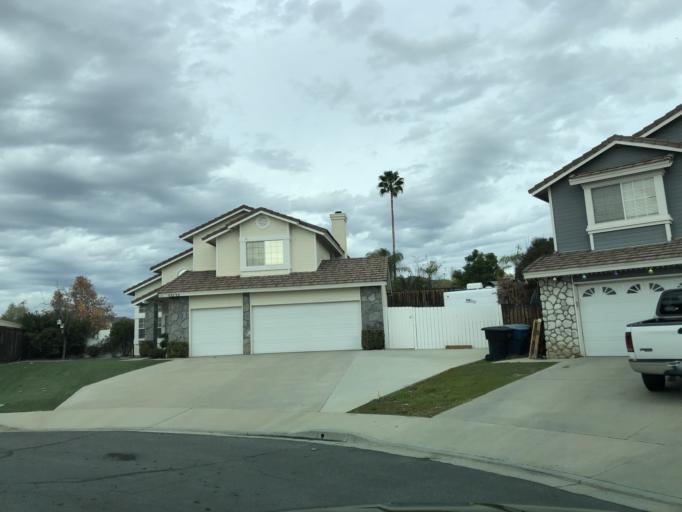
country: US
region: California
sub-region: Riverside County
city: Wildomar
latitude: 33.6100
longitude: -117.2630
